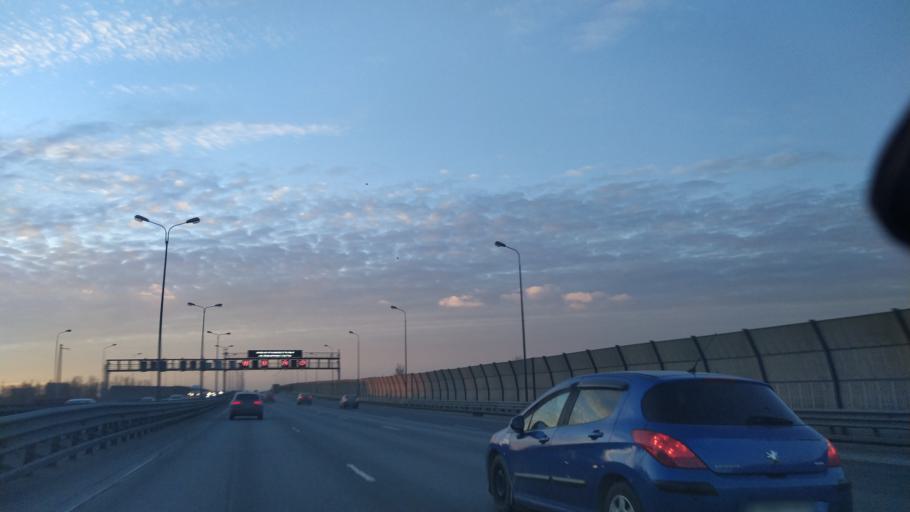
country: RU
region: St.-Petersburg
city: Krasnogvargeisky
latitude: 59.9747
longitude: 30.5403
